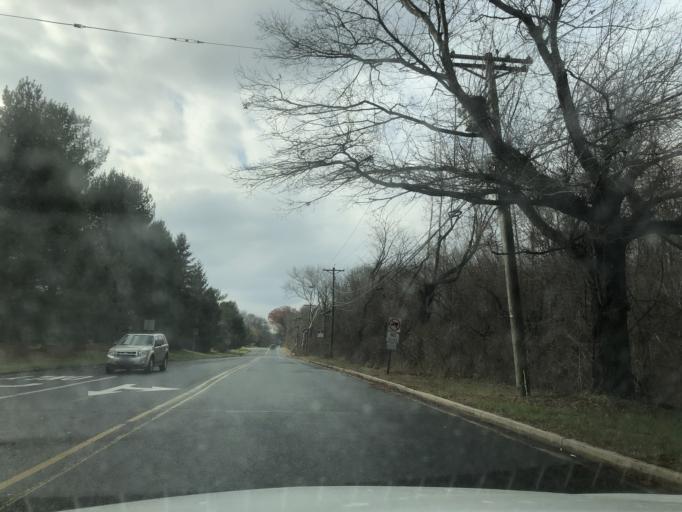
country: US
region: New Jersey
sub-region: Camden County
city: Bellmawr
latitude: 39.8474
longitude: -75.1067
